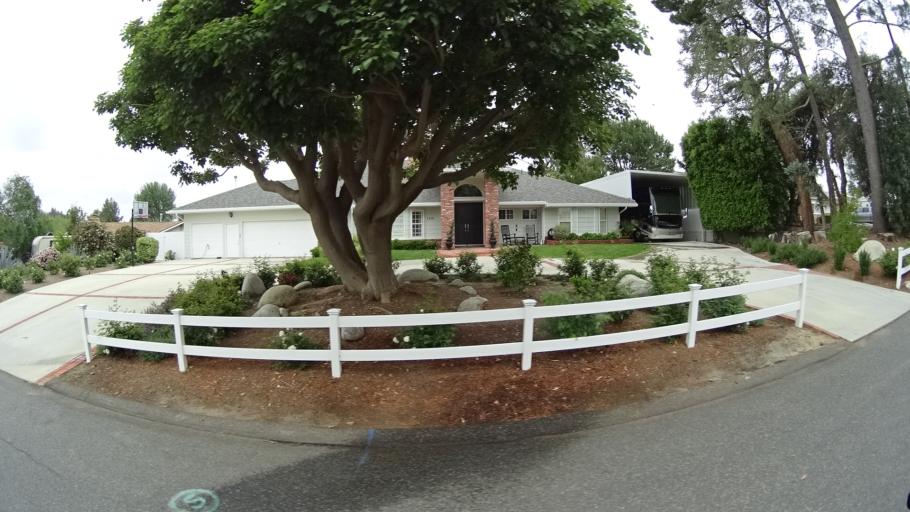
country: US
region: California
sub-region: Ventura County
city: Thousand Oaks
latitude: 34.2017
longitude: -118.8595
